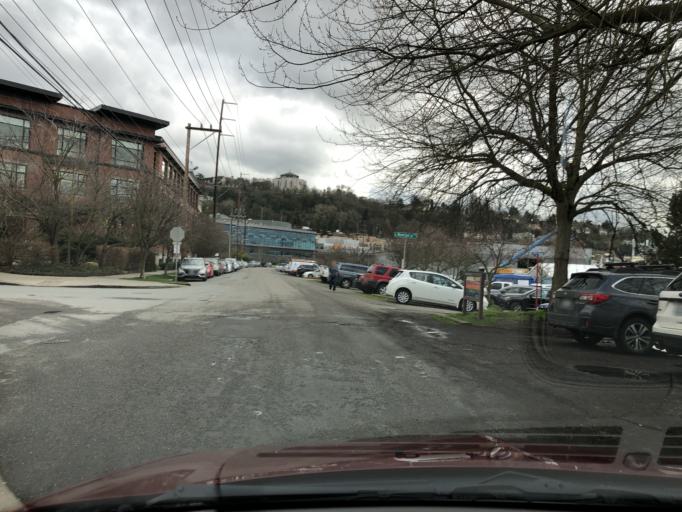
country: US
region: Washington
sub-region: King County
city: Seattle
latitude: 47.6369
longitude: -122.3291
